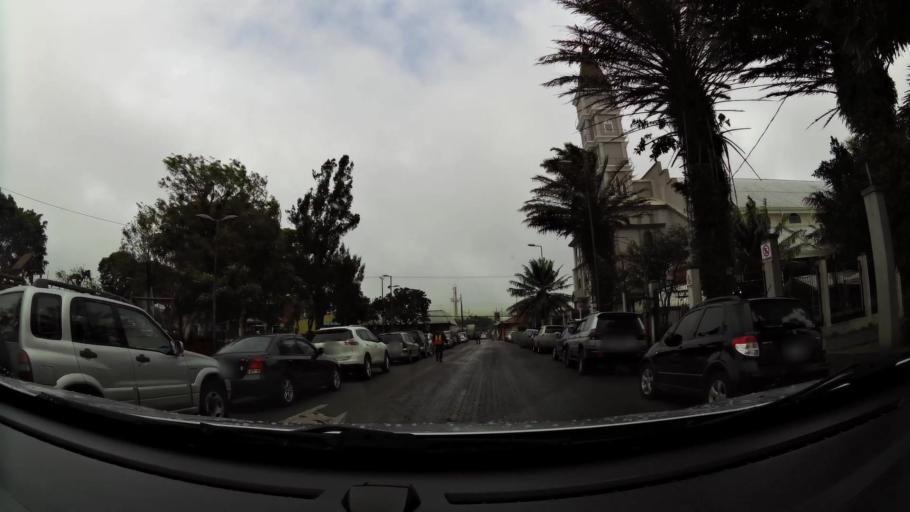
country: CR
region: Cartago
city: Paraiso
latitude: 9.8383
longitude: -83.8658
